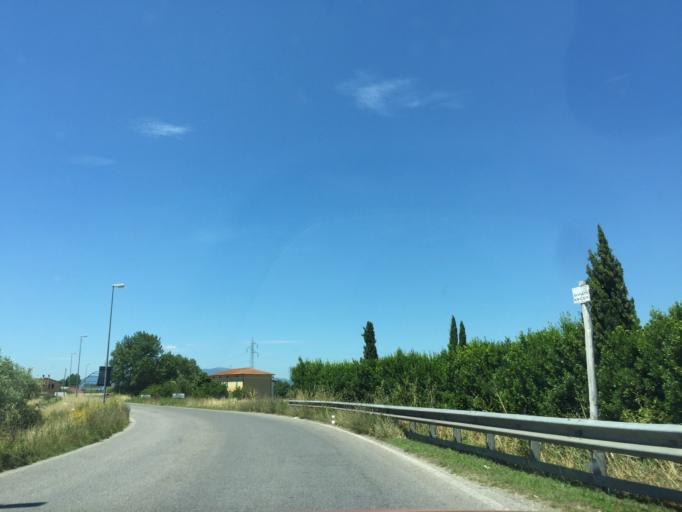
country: IT
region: Tuscany
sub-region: Province of Pisa
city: San Donato
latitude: 43.6898
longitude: 10.8048
